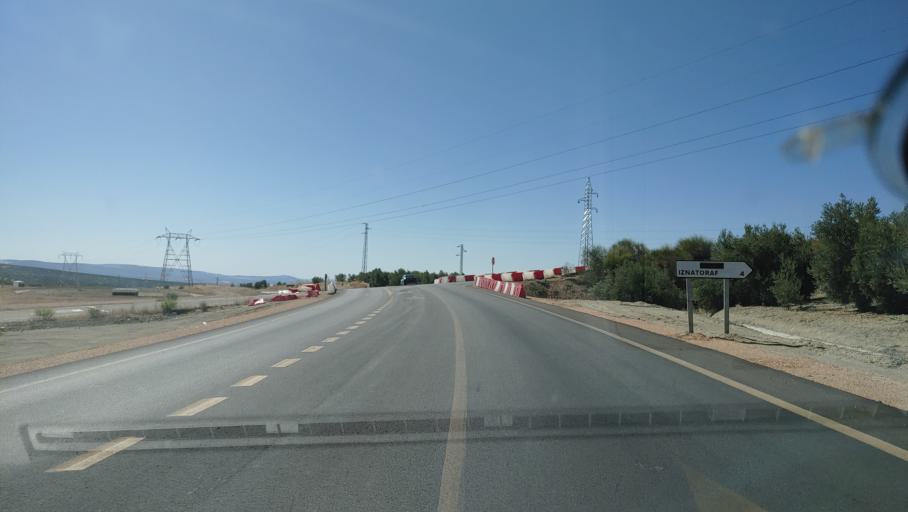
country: ES
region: Andalusia
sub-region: Provincia de Jaen
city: Iznatoraf
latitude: 38.1409
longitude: -3.0417
